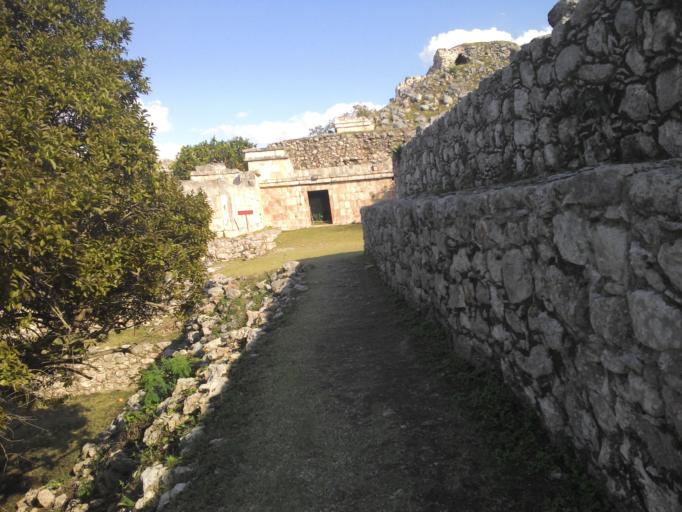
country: MX
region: Yucatan
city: Santa Elena
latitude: 20.2483
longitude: -89.6473
